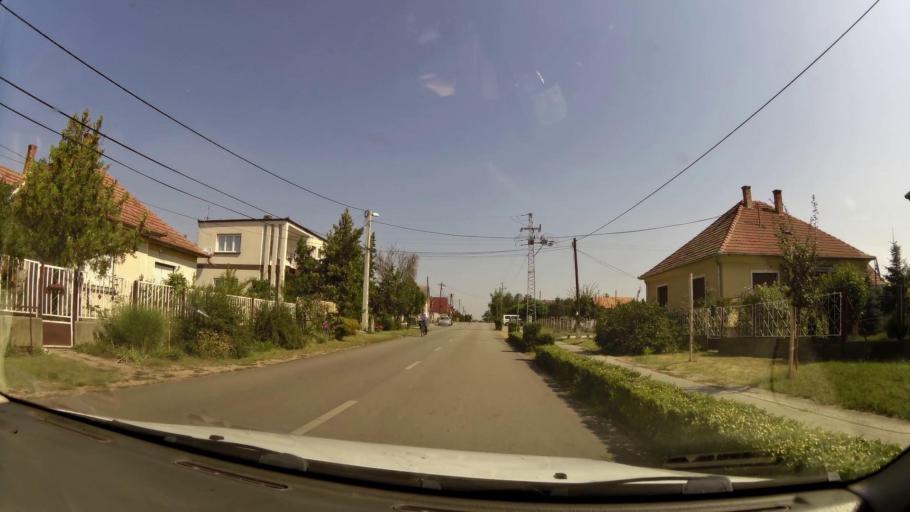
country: HU
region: Pest
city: Ujszilvas
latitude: 47.2676
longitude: 19.9133
